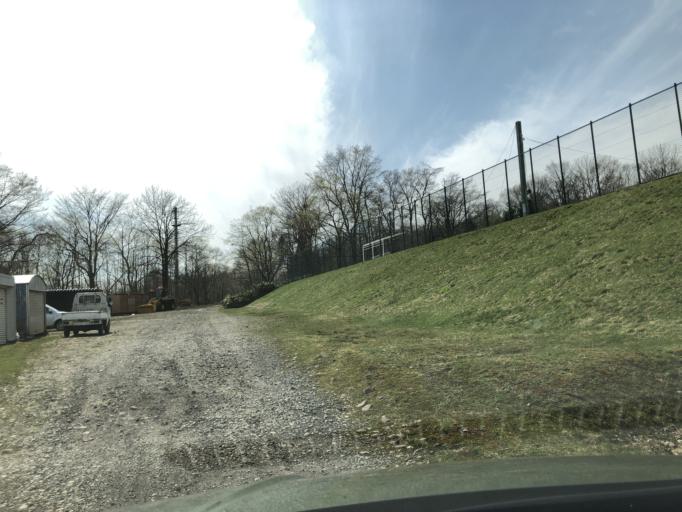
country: JP
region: Hokkaido
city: Akabira
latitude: 43.5934
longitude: 142.0463
